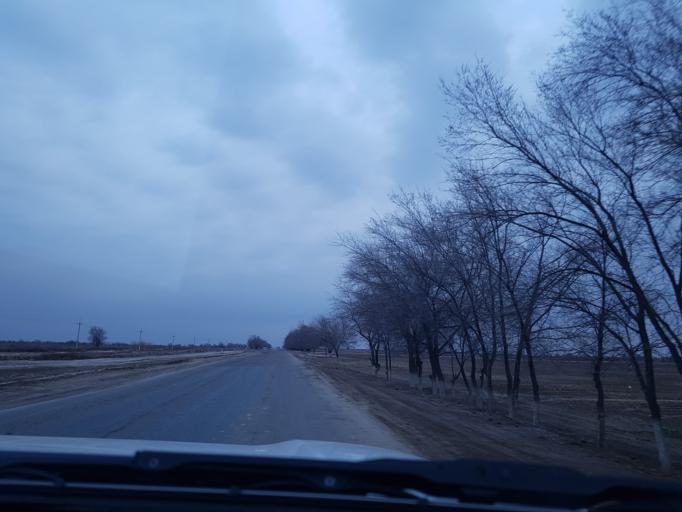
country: TM
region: Dasoguz
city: Yylanly
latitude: 41.9284
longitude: 59.5592
